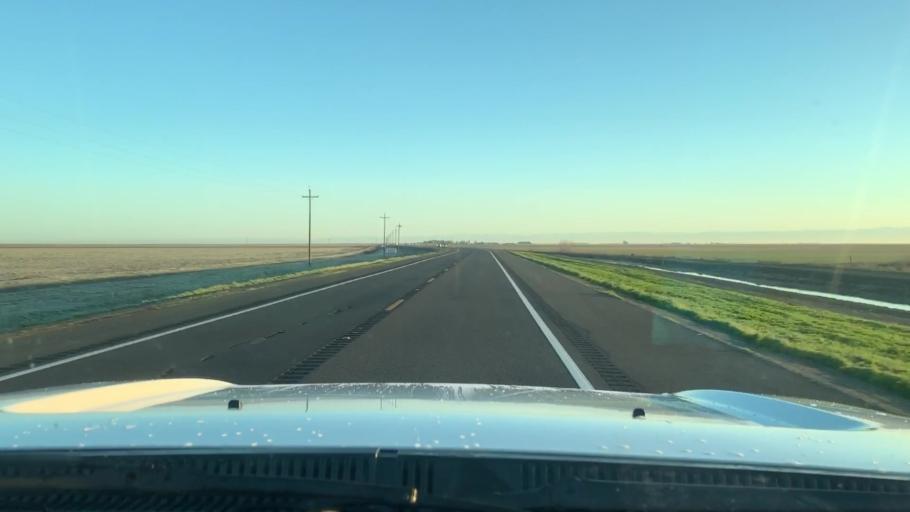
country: US
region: California
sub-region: Kings County
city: Kettleman City
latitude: 36.0865
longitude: -119.9157
